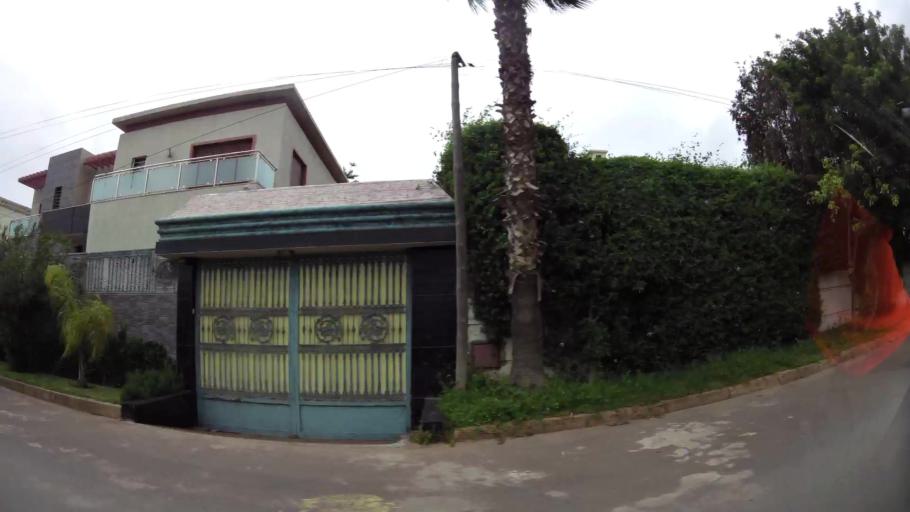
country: MA
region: Grand Casablanca
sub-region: Casablanca
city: Casablanca
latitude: 33.5452
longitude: -7.6392
